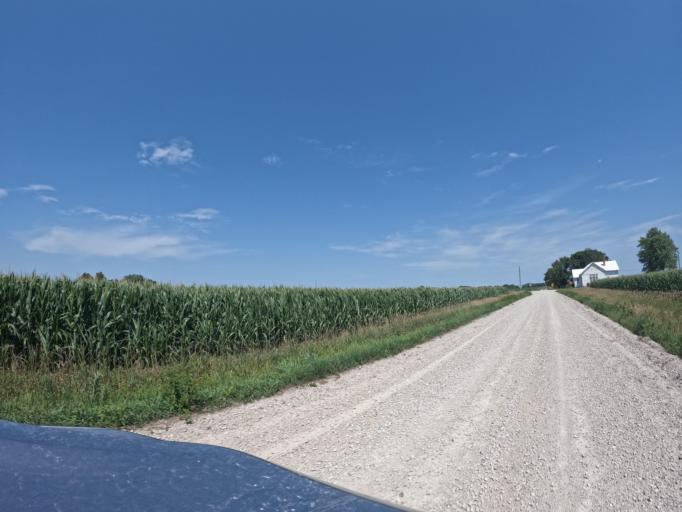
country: US
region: Iowa
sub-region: Henry County
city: Mount Pleasant
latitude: 40.9013
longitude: -91.6327
